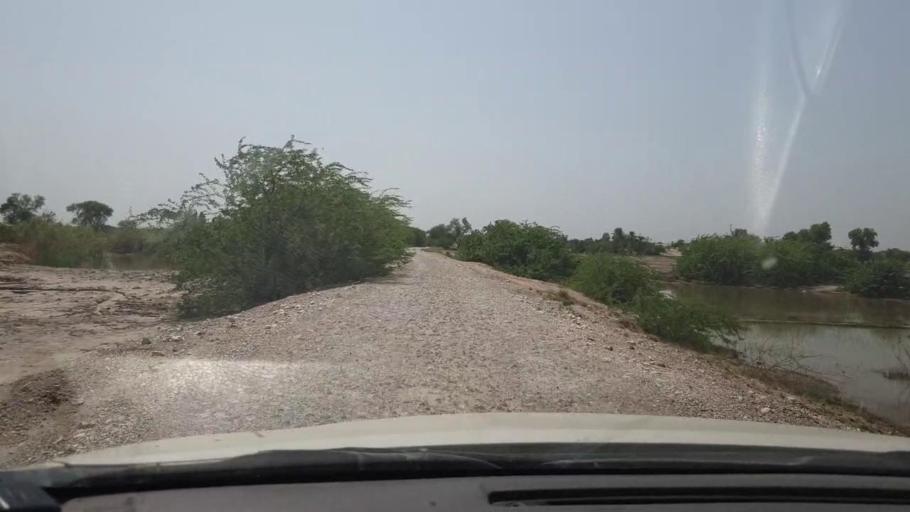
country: PK
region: Sindh
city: Rohri
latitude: 27.5212
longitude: 69.0947
